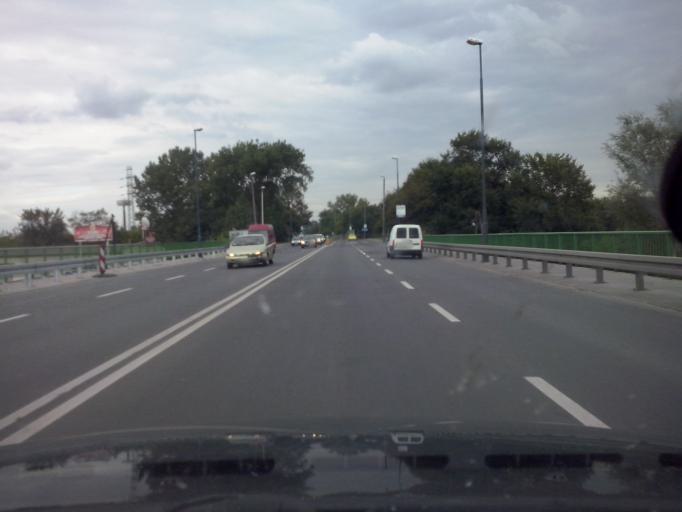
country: PL
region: Lesser Poland Voivodeship
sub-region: Krakow
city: Krakow
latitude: 50.0552
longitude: 19.9975
